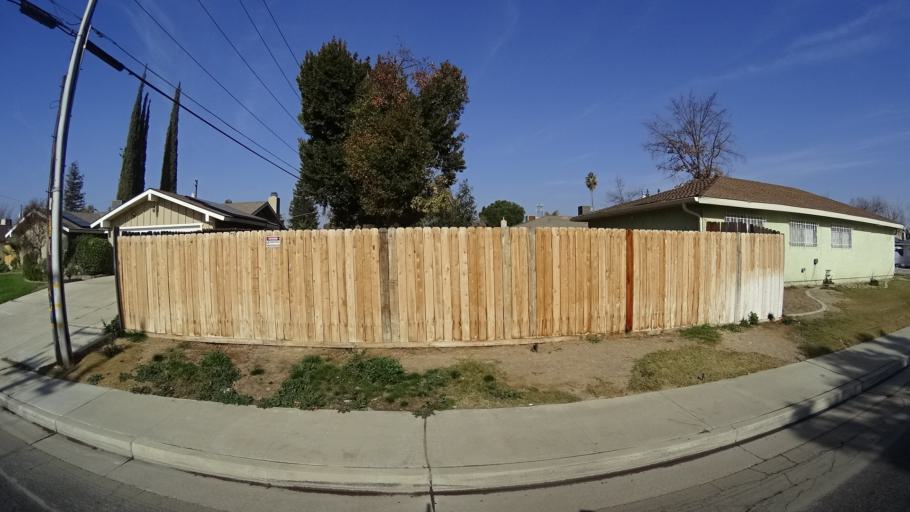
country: US
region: California
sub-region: Kern County
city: Bakersfield
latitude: 35.3286
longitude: -119.0456
